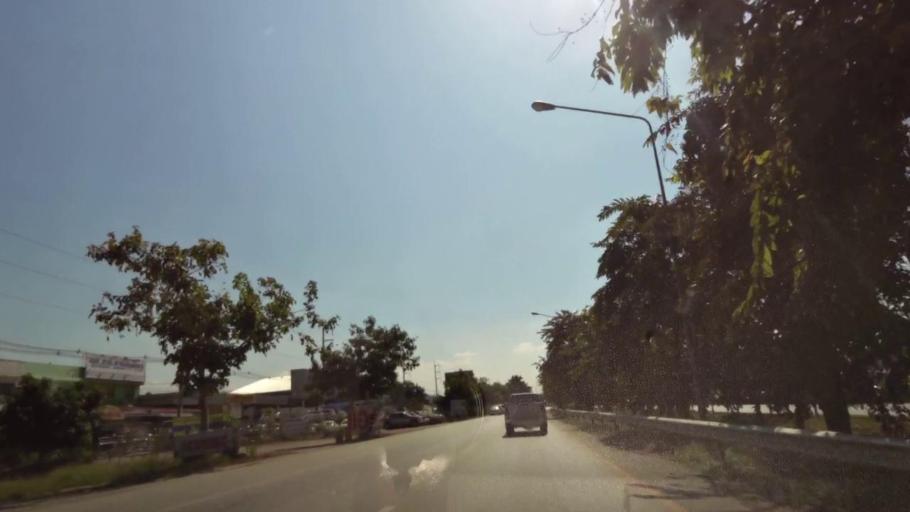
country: TH
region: Nakhon Sawan
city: Nakhon Sawan
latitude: 15.7447
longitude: 100.1222
